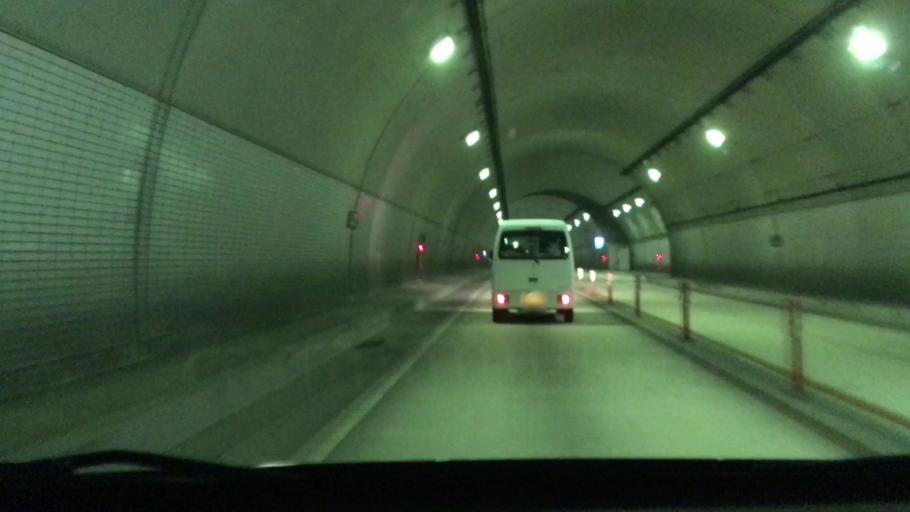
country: JP
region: Nagasaki
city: Sasebo
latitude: 33.0907
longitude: 129.7785
